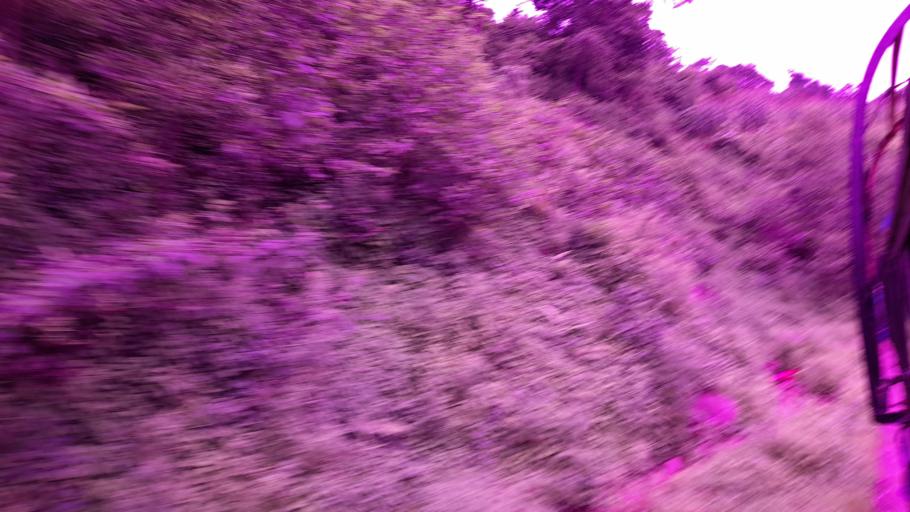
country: NP
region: Central Region
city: Kirtipur
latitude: 27.8245
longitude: 85.2099
